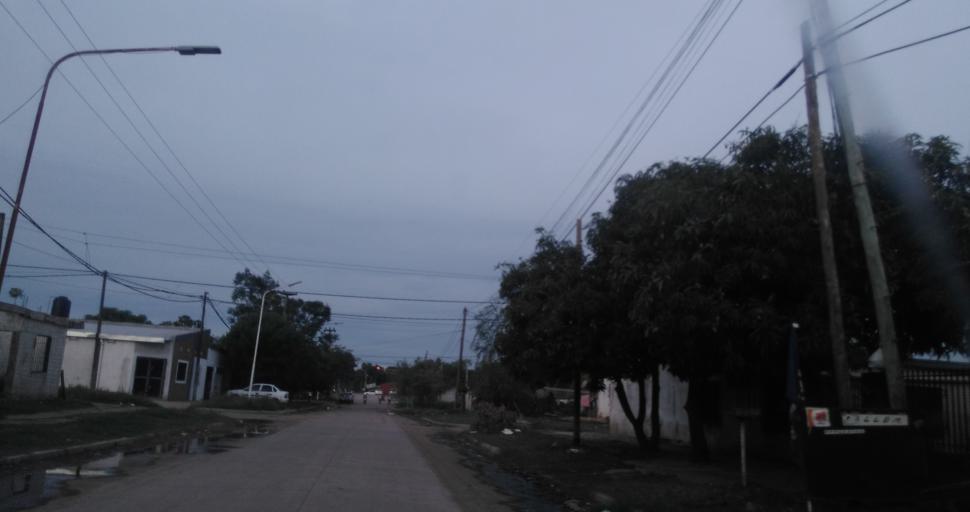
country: AR
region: Chaco
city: Fontana
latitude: -27.4223
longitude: -59.0365
